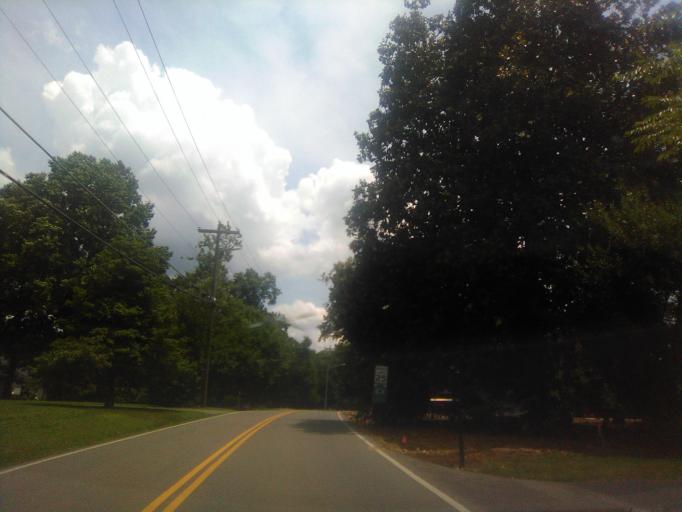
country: US
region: Tennessee
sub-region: Davidson County
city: Belle Meade
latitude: 36.0905
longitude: -86.8665
